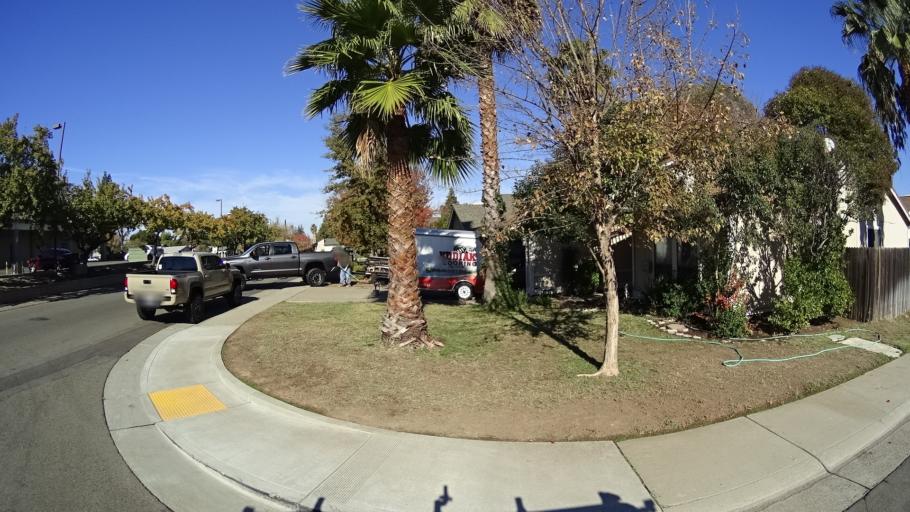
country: US
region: California
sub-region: Sacramento County
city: Antelope
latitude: 38.7093
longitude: -121.3113
